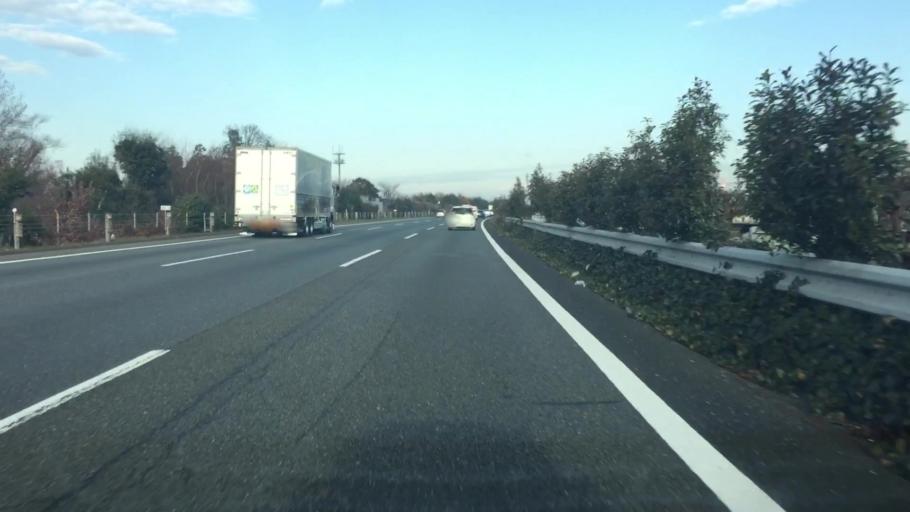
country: JP
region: Saitama
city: Yorii
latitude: 36.1372
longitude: 139.2283
